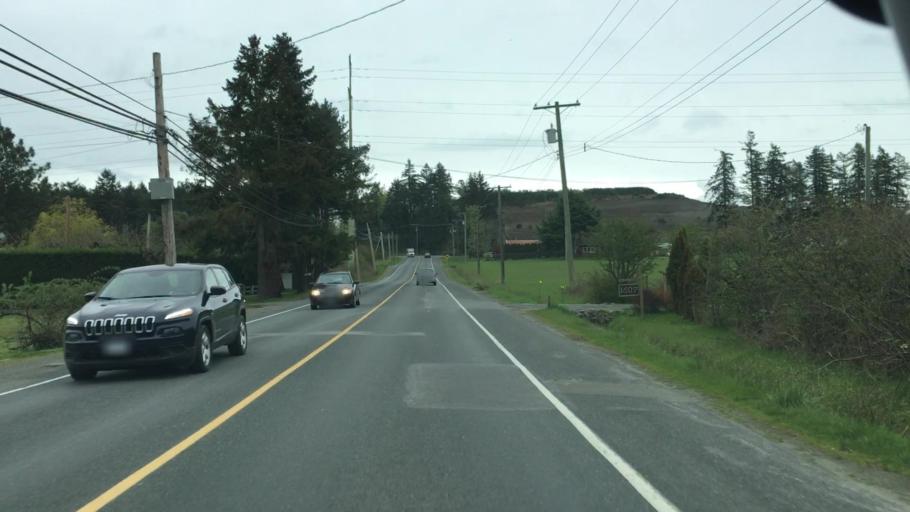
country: CA
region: British Columbia
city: North Saanich
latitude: 48.5651
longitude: -123.4326
